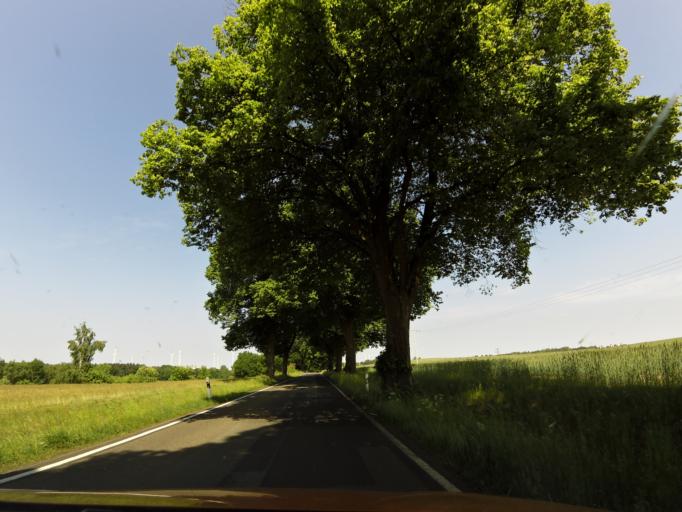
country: DE
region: Mecklenburg-Vorpommern
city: Neuburg
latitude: 53.4008
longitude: 11.9241
